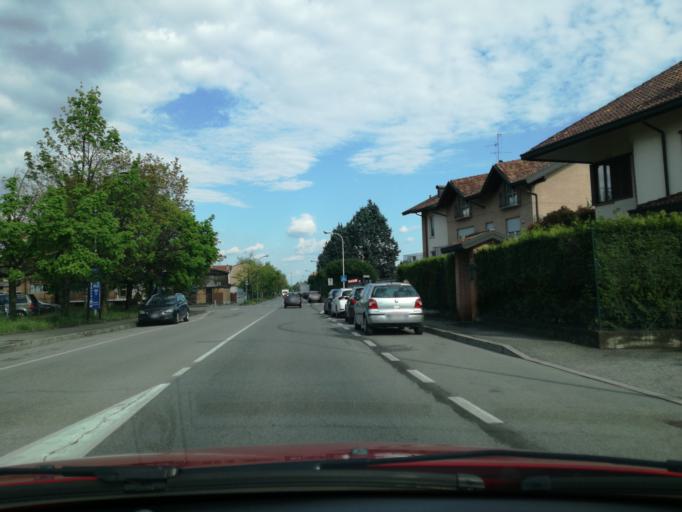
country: IT
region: Lombardy
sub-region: Provincia di Monza e Brianza
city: Seregno
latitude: 45.6556
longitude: 9.2135
